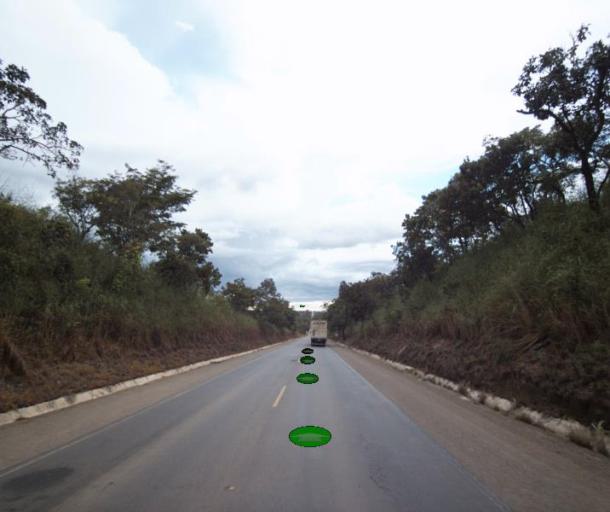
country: BR
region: Goias
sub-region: Itapaci
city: Itapaci
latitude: -14.8212
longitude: -49.2980
